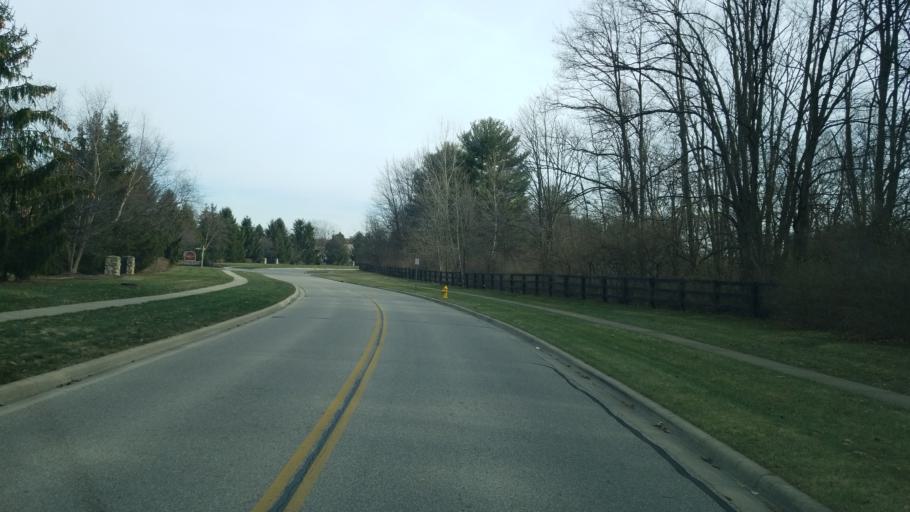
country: US
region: Ohio
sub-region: Delaware County
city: Lewis Center
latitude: 40.1671
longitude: -83.0275
